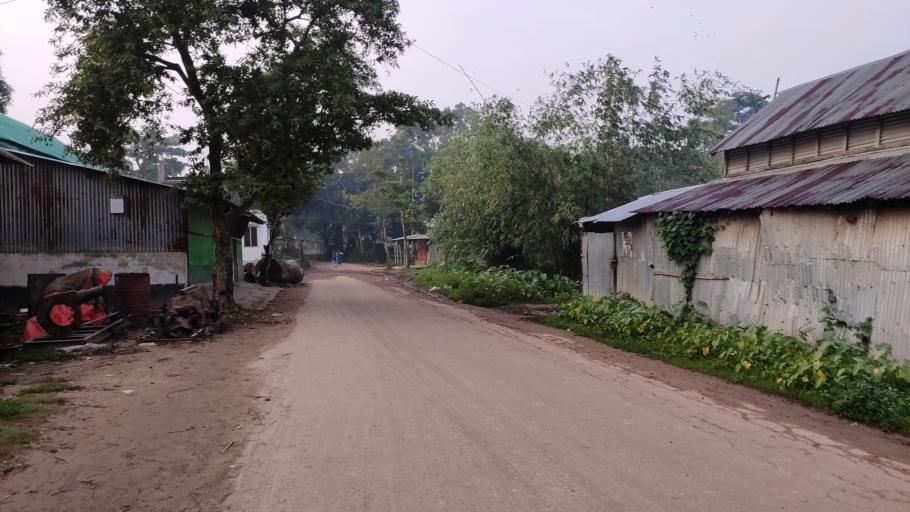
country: BD
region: Dhaka
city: Netrakona
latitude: 24.7137
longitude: 90.9468
